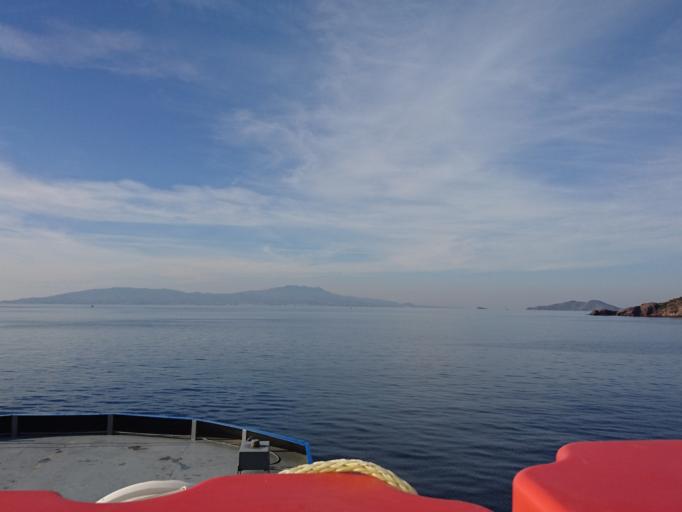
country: TR
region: Mugla
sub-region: Bodrum
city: Bodrum
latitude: 36.9934
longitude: 27.3952
